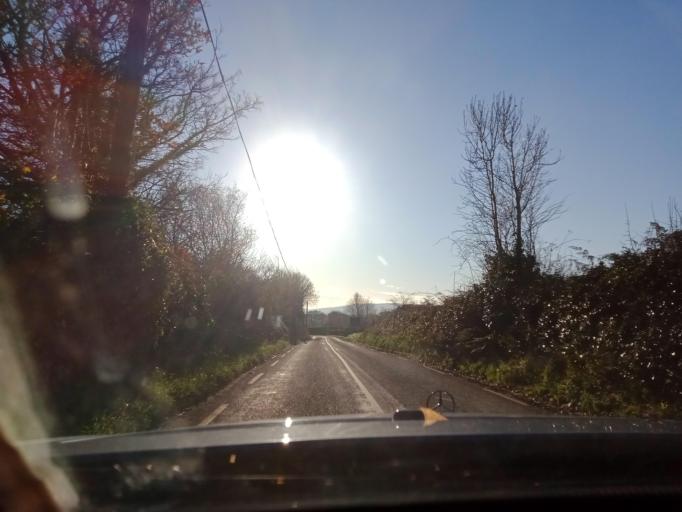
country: IE
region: Leinster
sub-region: Kilkenny
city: Piltown
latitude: 52.3923
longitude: -7.3490
